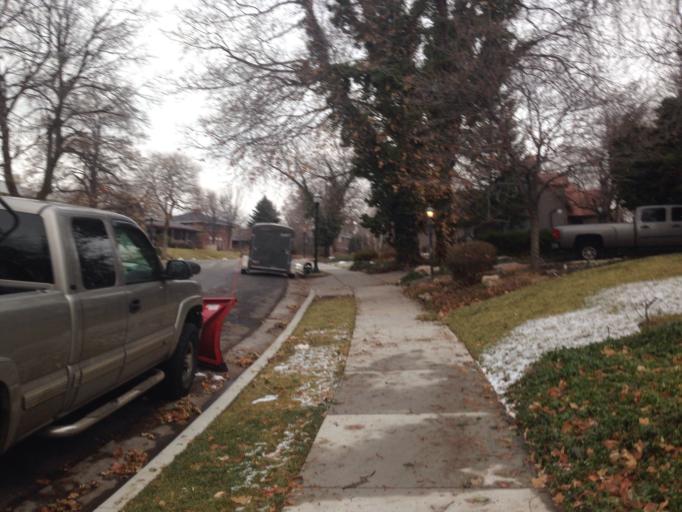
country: US
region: Utah
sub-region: Salt Lake County
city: Willard
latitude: 40.7461
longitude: -111.8499
